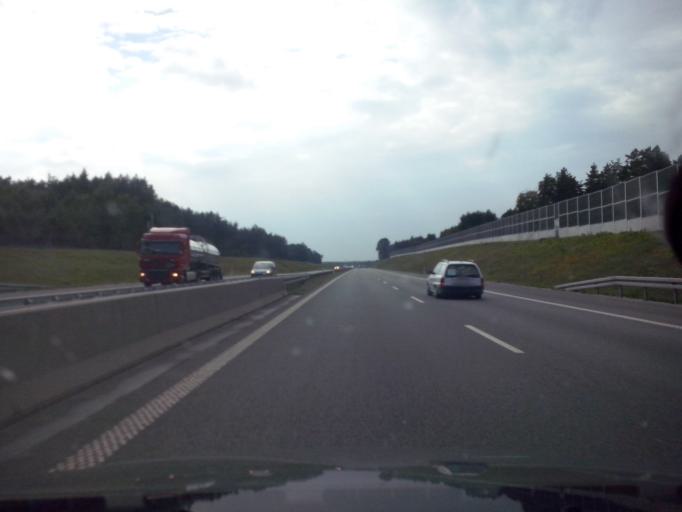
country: PL
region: Lesser Poland Voivodeship
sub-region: Powiat brzeski
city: Przyborow
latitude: 50.0012
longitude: 20.6470
